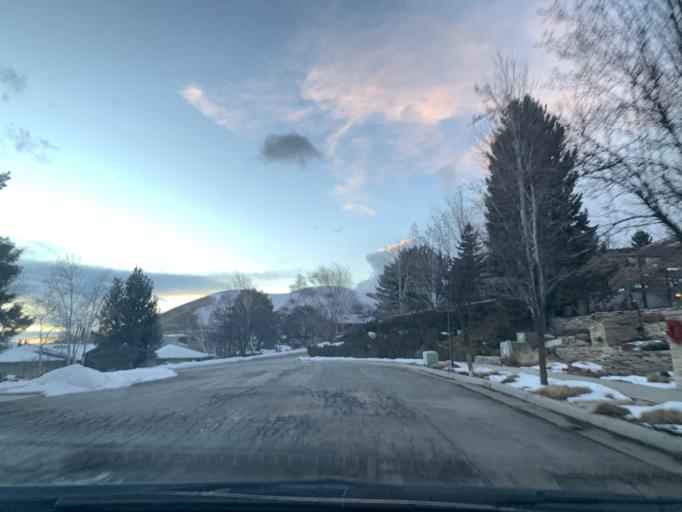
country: US
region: Utah
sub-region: Salt Lake County
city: Salt Lake City
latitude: 40.7843
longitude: -111.8515
